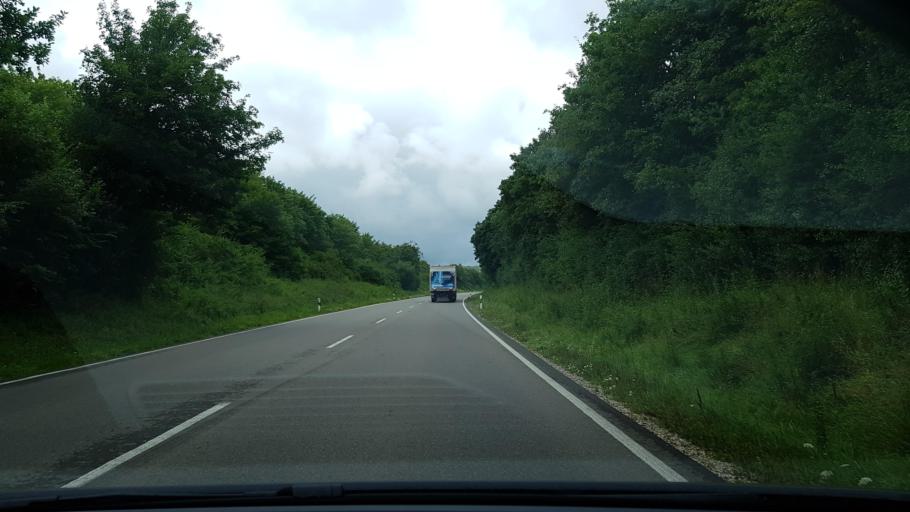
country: DE
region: Baden-Wuerttemberg
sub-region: Tuebingen Region
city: Westerheim
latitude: 48.4723
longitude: 9.6076
